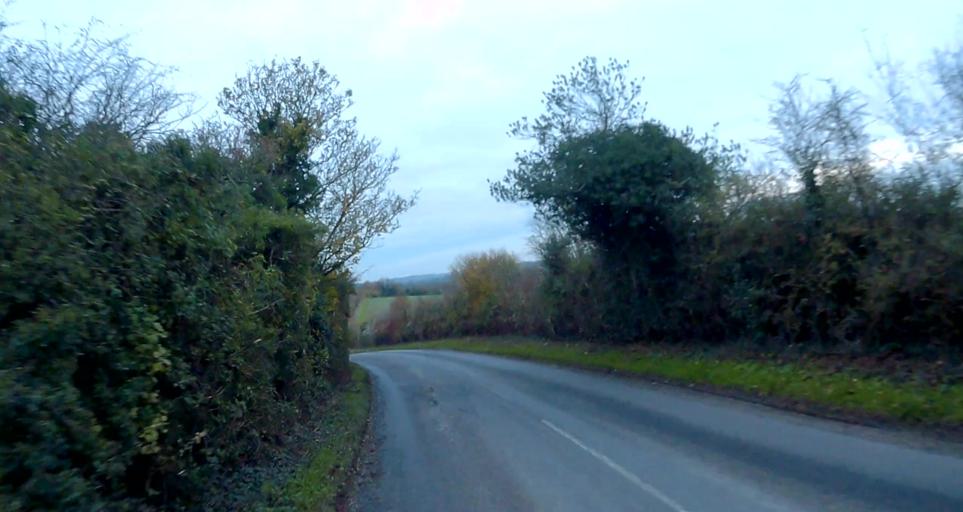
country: GB
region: England
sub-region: Hampshire
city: Odiham
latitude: 51.2488
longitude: -0.9682
